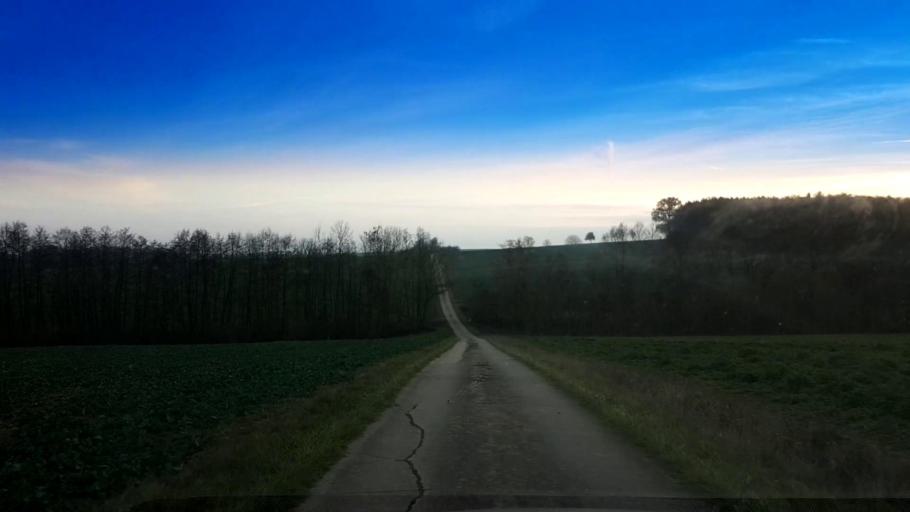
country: DE
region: Bavaria
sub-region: Upper Franconia
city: Schesslitz
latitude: 49.9797
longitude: 10.9802
